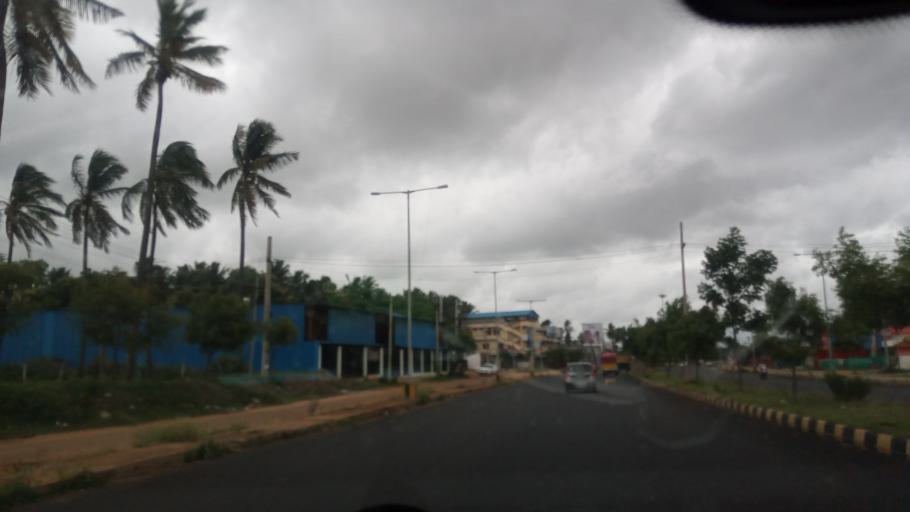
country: IN
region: Karnataka
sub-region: Mysore
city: Mysore
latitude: 12.3027
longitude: 76.6021
